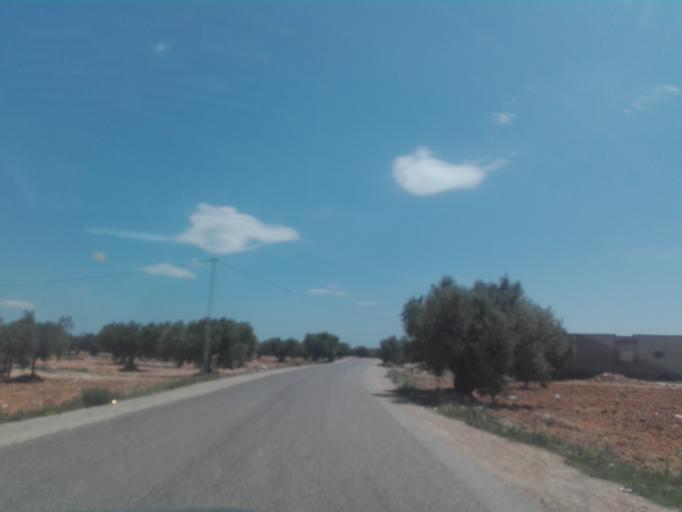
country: TN
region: Safaqis
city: Sfax
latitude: 34.6240
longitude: 10.6055
